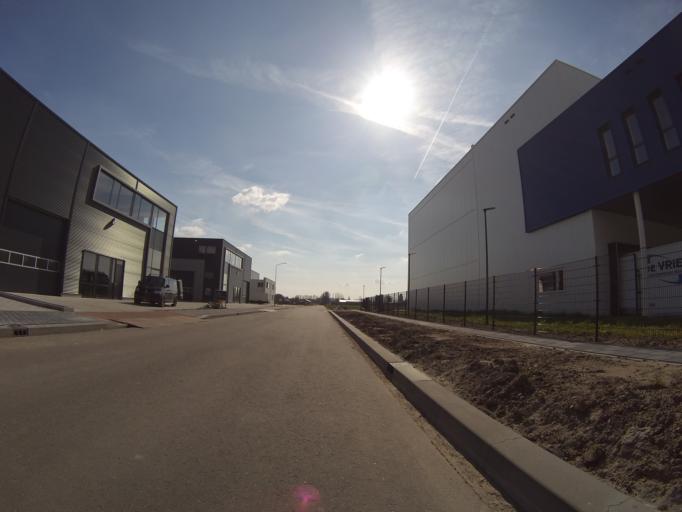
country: NL
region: Gelderland
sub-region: Gemeente Nijkerk
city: Nijkerk
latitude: 52.2075
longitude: 5.4499
